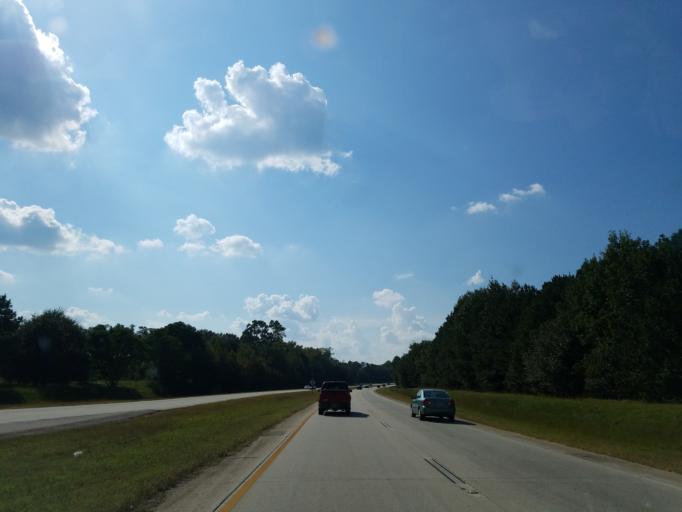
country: US
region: Georgia
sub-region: Oconee County
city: Bogart
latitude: 33.9174
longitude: -83.4830
